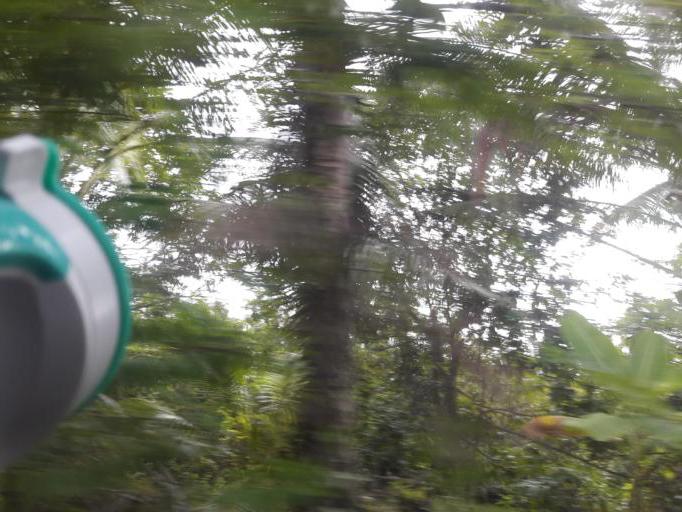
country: TH
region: Ratchaburi
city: Damnoen Saduak
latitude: 13.5367
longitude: 100.0054
